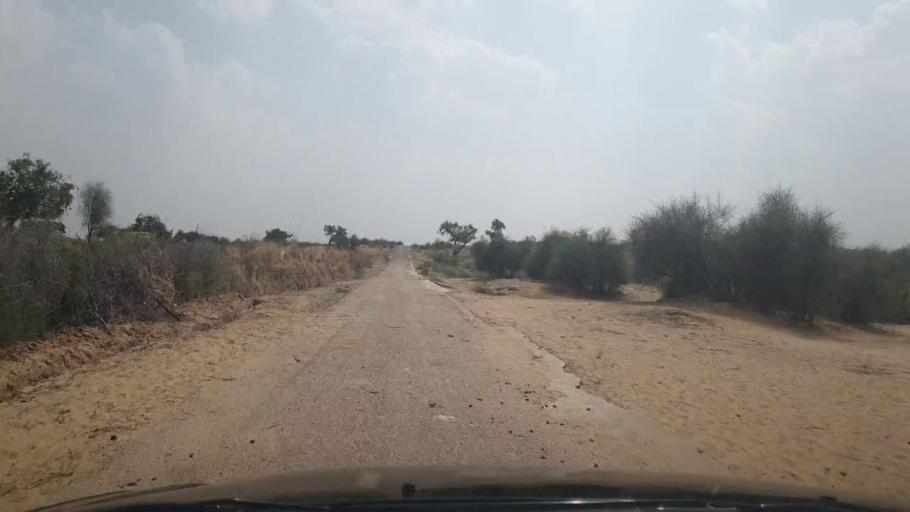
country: PK
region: Sindh
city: Islamkot
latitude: 25.0098
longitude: 70.5276
